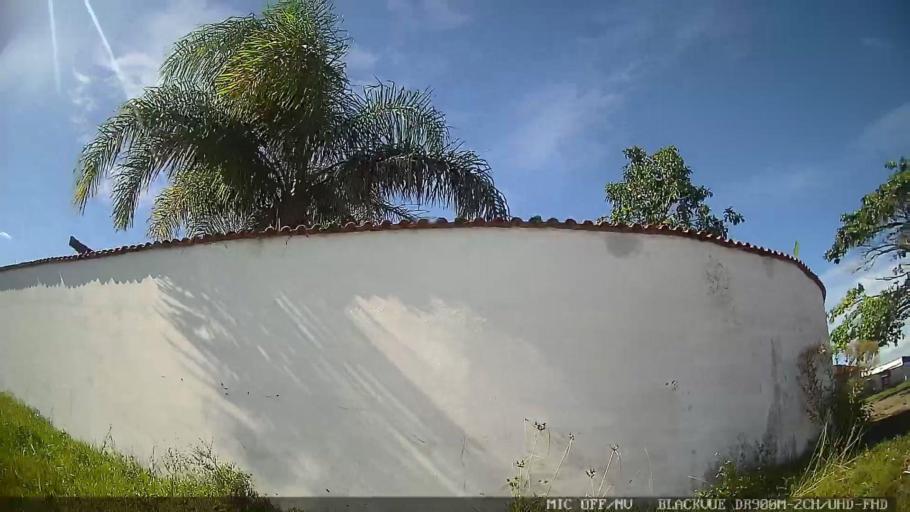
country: BR
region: Sao Paulo
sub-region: Itanhaem
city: Itanhaem
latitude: -24.2360
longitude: -46.8935
